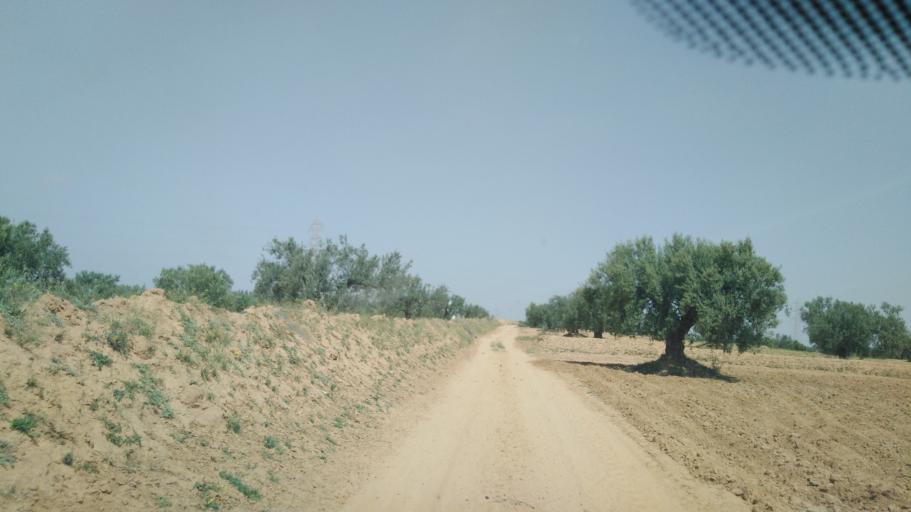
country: TN
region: Safaqis
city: Sfax
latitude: 34.7388
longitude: 10.5723
